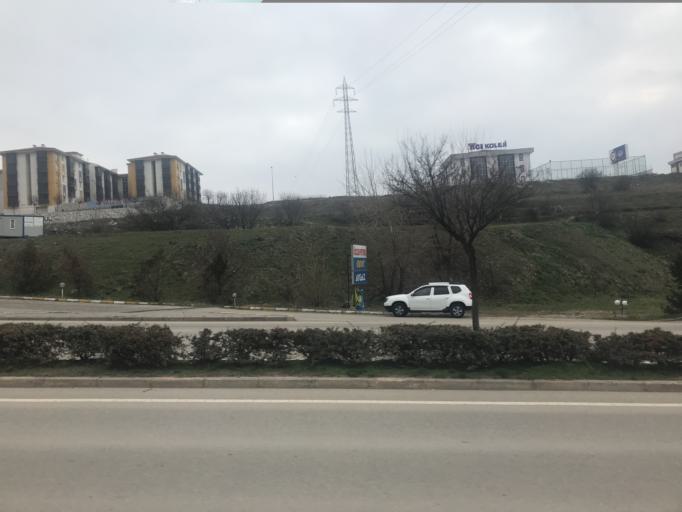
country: TR
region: Karabuk
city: Safranbolu
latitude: 41.2371
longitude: 32.6739
